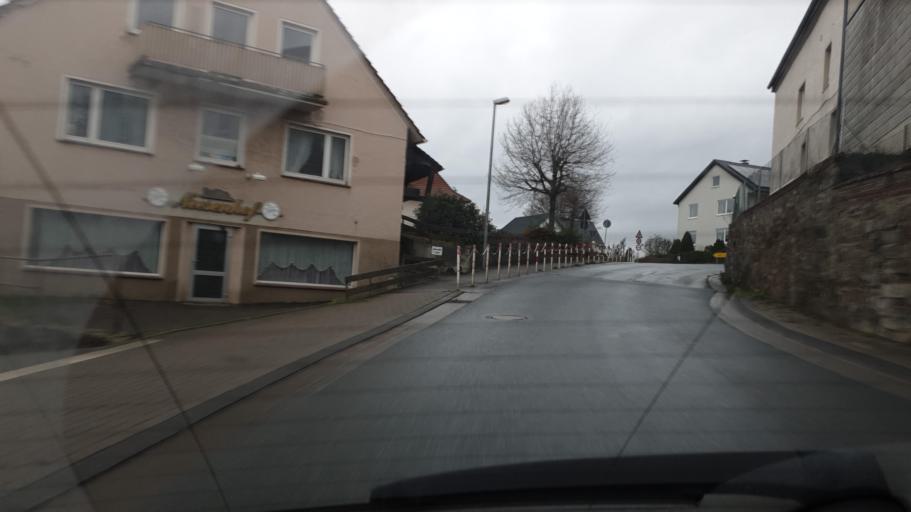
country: DE
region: North Rhine-Westphalia
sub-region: Regierungsbezirk Detmold
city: Detmold
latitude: 51.9796
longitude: 8.8451
